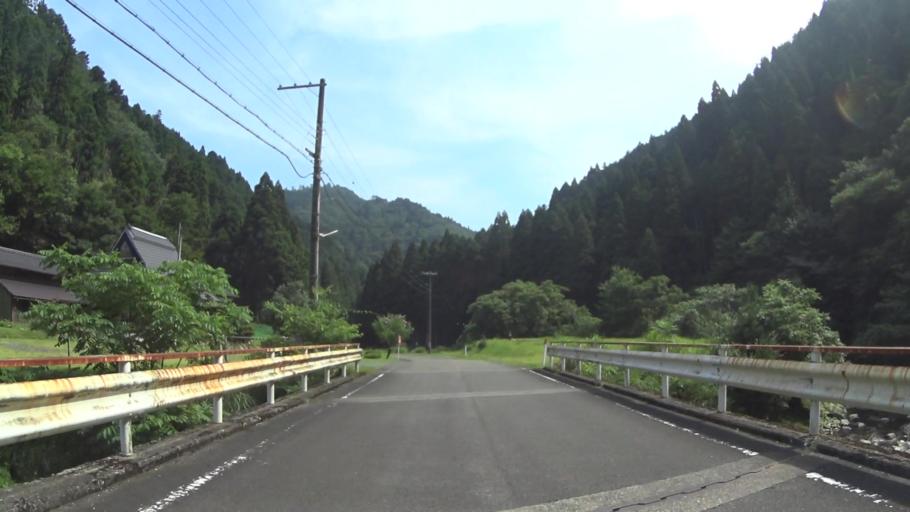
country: JP
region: Fukui
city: Obama
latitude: 35.3316
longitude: 135.6453
